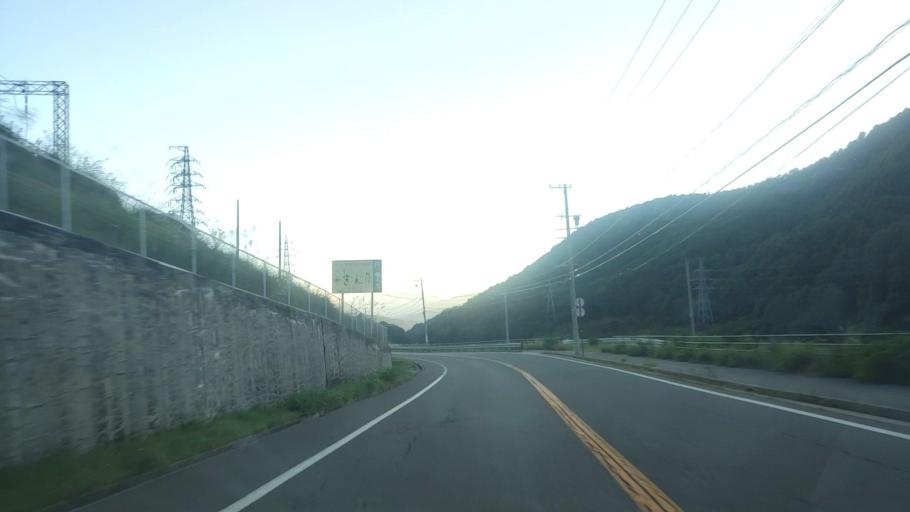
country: JP
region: Nagano
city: Suwa
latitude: 36.1071
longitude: 138.0973
